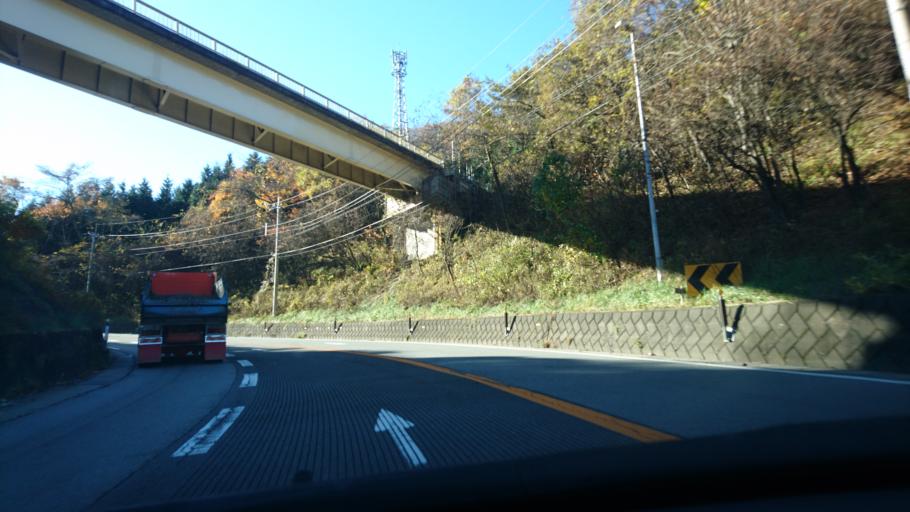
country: JP
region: Nagano
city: Saku
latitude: 36.3157
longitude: 138.6512
